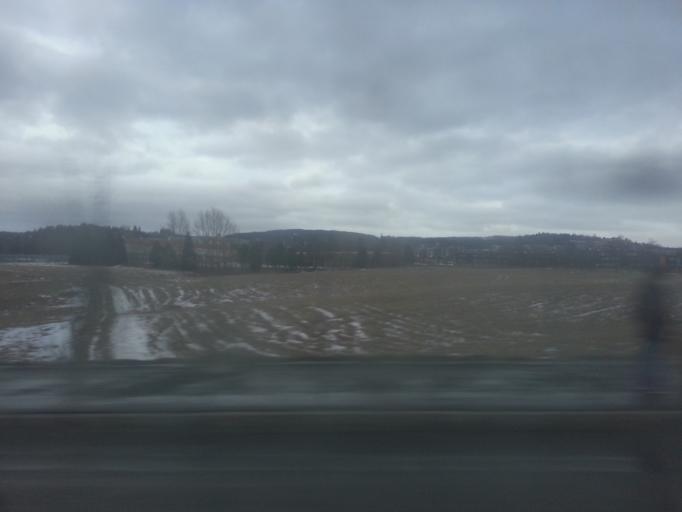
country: NO
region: Sor-Trondelag
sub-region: Trondheim
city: Trondheim
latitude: 63.4221
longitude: 10.4505
